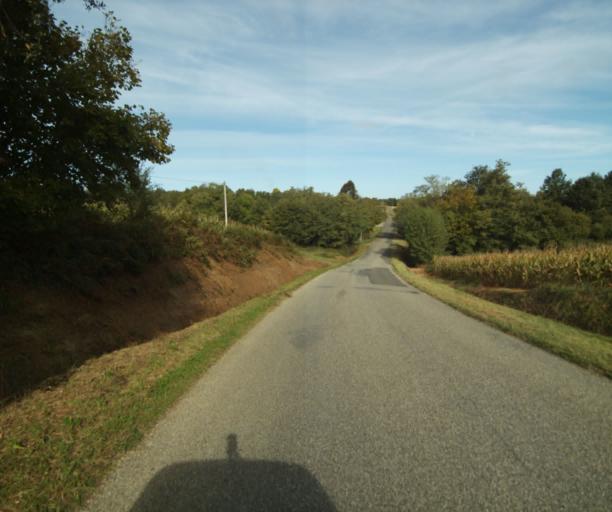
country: FR
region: Midi-Pyrenees
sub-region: Departement du Gers
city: Eauze
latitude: 43.8977
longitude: 0.1382
